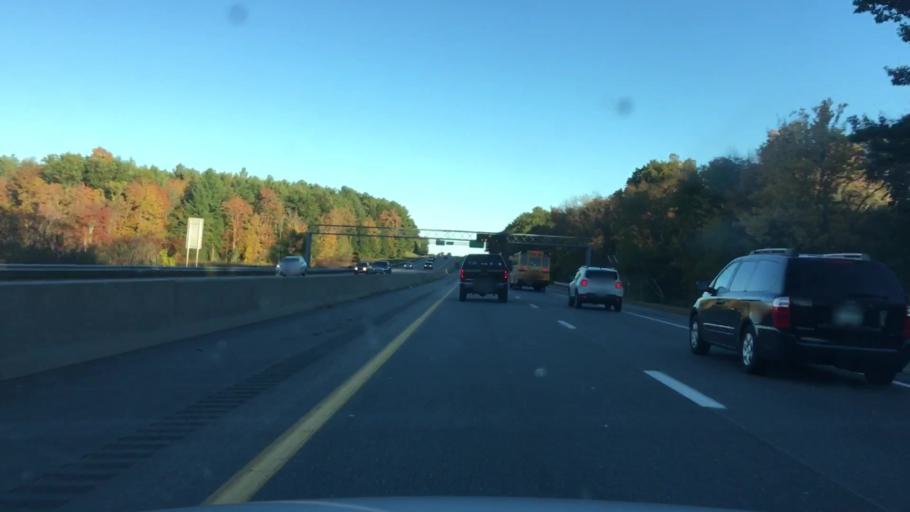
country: US
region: New Hampshire
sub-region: Rockingham County
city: Hampton
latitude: 42.9647
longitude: -70.8780
